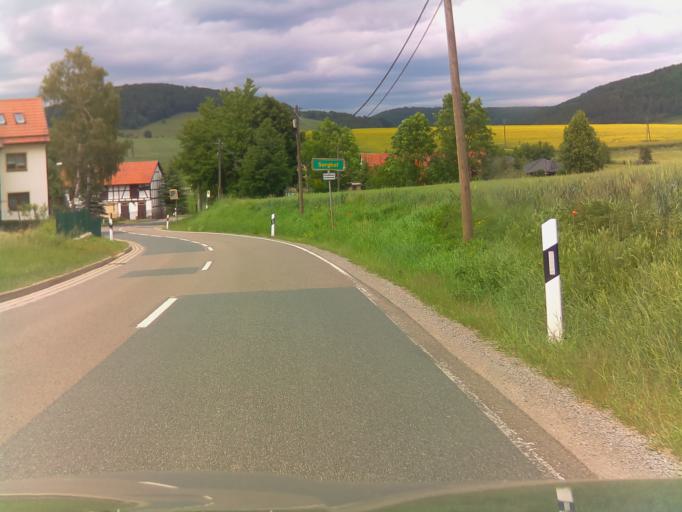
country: DE
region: Thuringia
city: Henneberg
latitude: 50.5099
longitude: 10.3199
